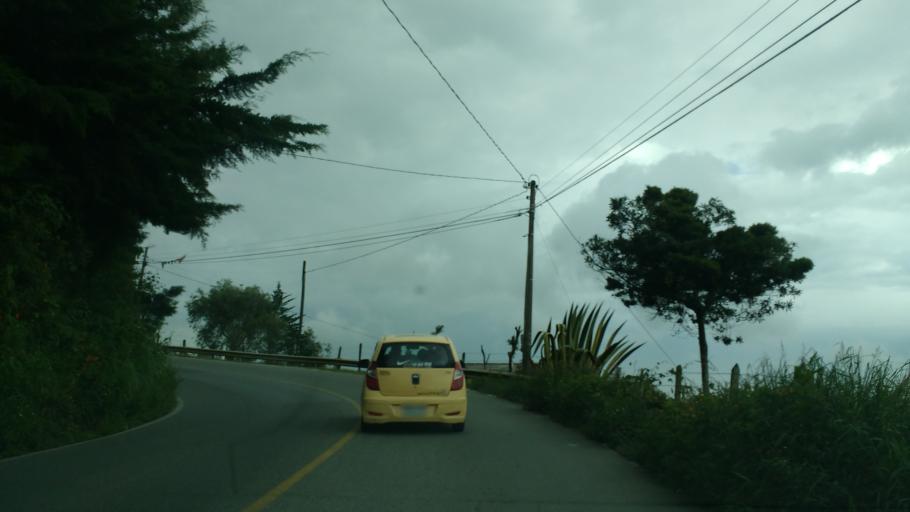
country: CO
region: Antioquia
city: Marinilla
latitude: 6.1856
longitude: -75.3044
